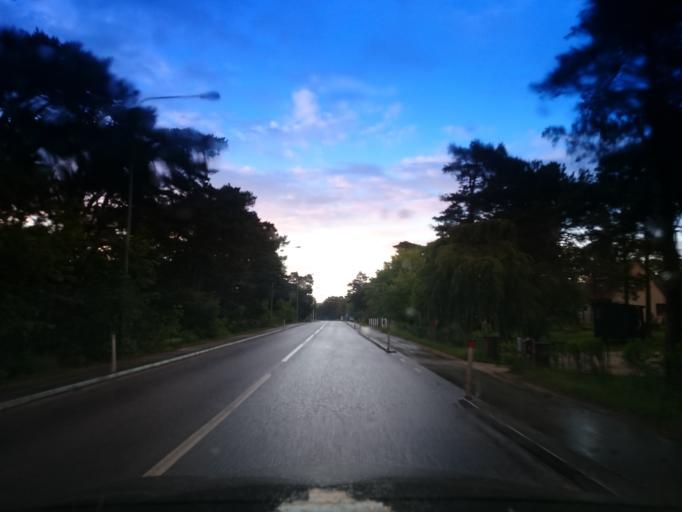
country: SE
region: Gotland
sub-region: Gotland
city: Visby
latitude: 57.6603
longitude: 18.3295
